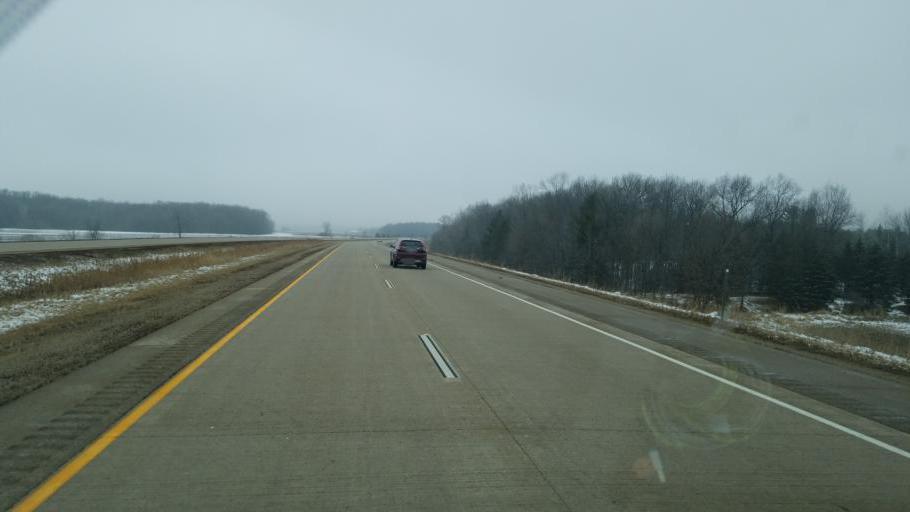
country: US
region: Wisconsin
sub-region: Winnebago County
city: Winneconne
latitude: 44.2343
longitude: -88.7669
